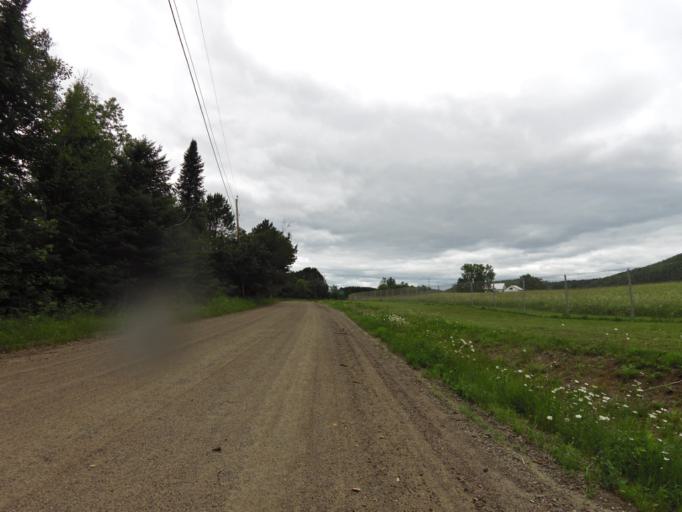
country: CA
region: Ontario
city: Hawkesbury
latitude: 45.9025
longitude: -74.6501
